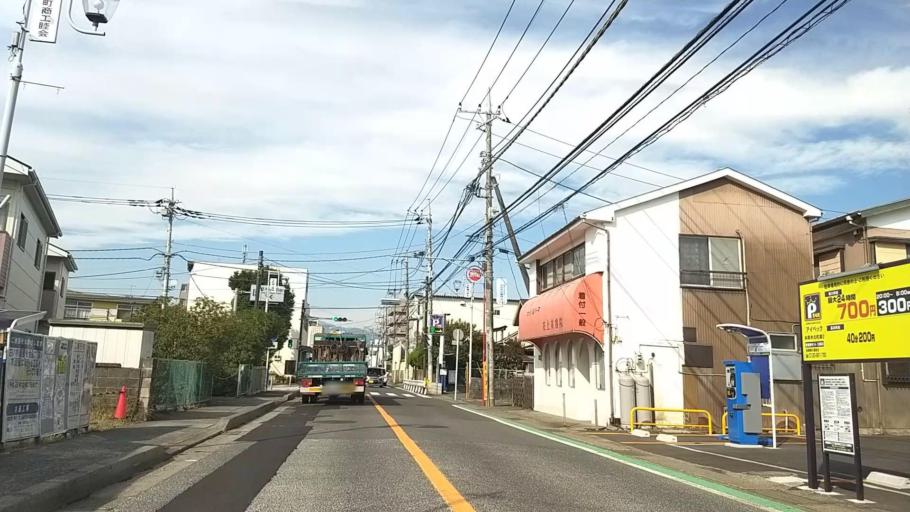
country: JP
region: Kanagawa
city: Atsugi
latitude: 35.4476
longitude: 139.3647
